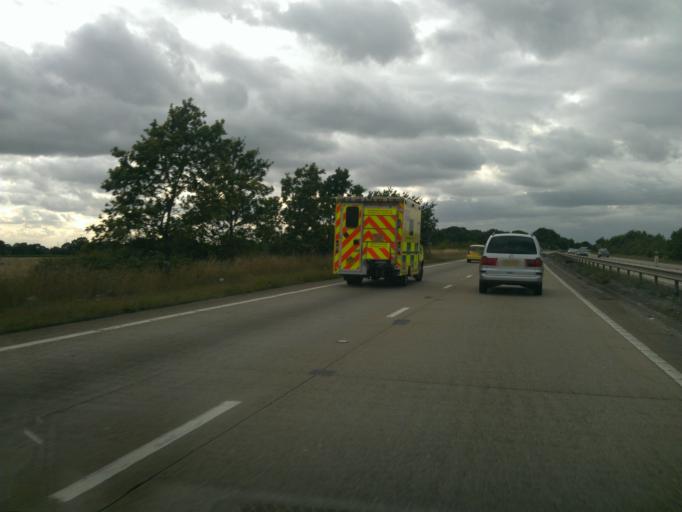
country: GB
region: England
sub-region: Essex
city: Alresford
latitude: 51.8982
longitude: 0.9890
